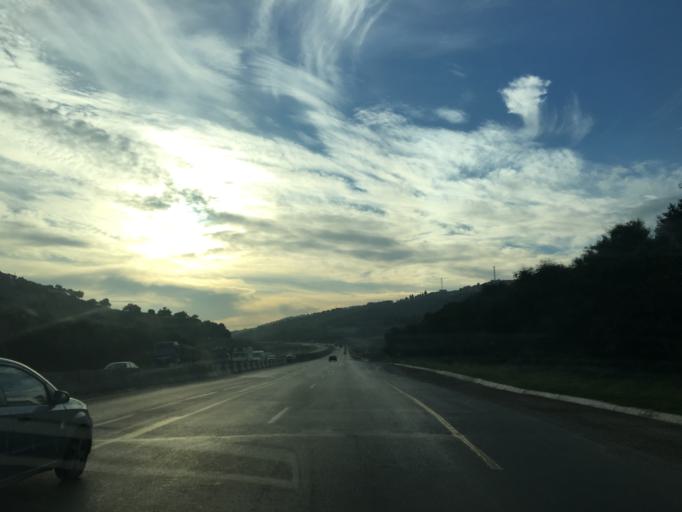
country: DZ
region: Bouira
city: Draa el Mizan
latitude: 36.4663
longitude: 3.7670
